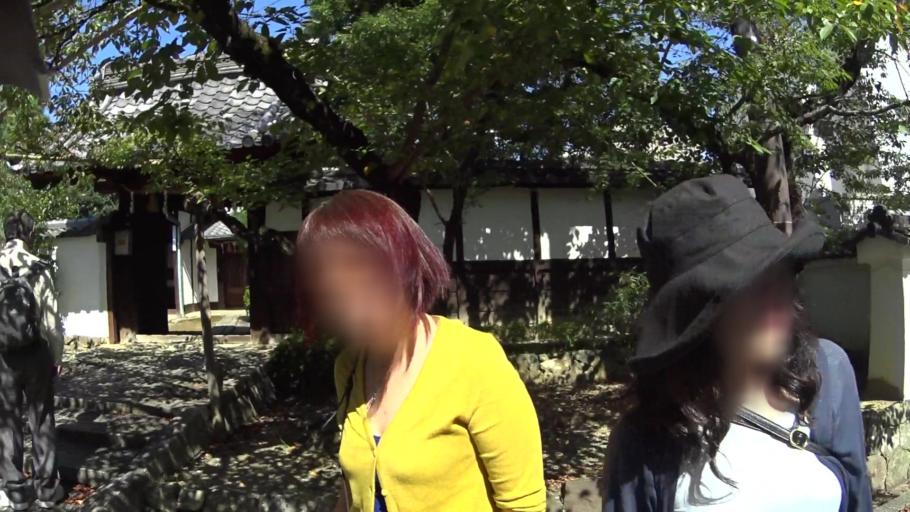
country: JP
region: Kyoto
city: Muko
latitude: 34.9443
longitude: 135.7003
